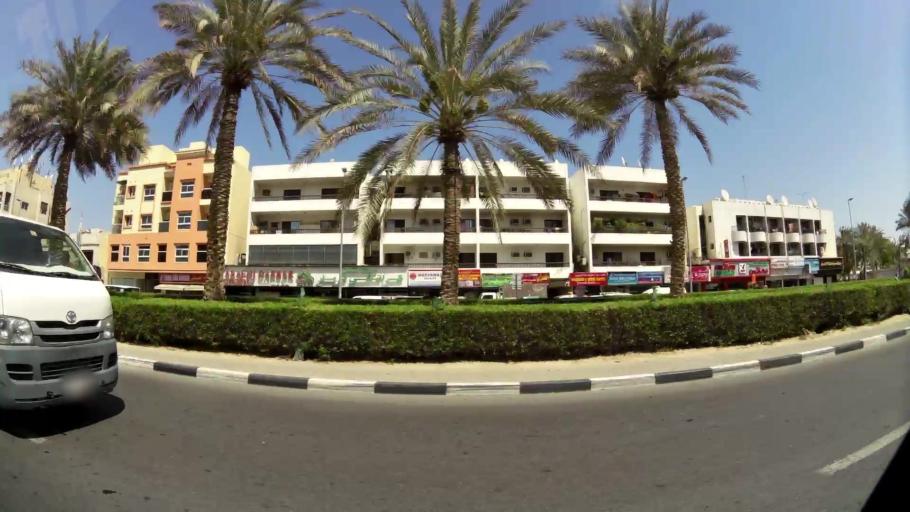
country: AE
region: Ash Shariqah
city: Sharjah
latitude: 25.2265
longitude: 55.2736
